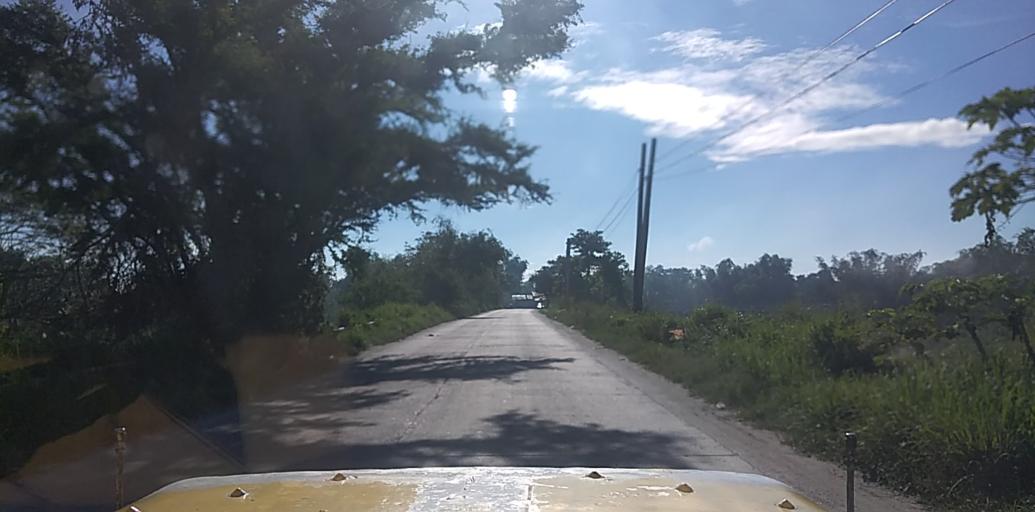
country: PH
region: Central Luzon
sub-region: Province of Pampanga
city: Anao
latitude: 15.1200
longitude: 120.7019
